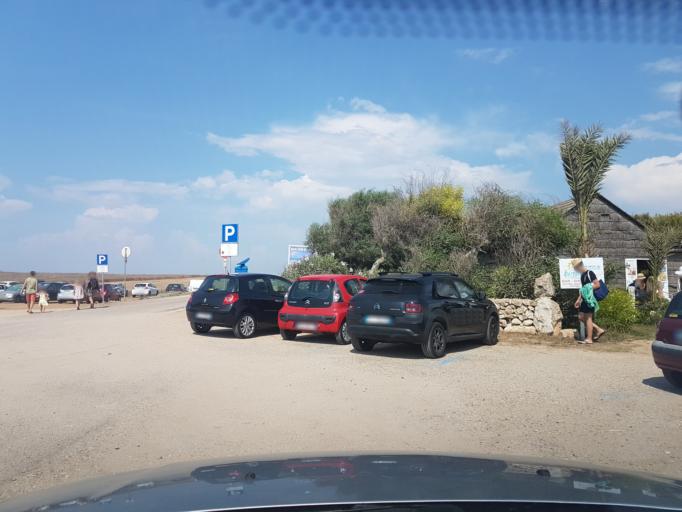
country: IT
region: Sardinia
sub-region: Provincia di Oristano
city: Cabras
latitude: 39.9688
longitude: 8.4003
